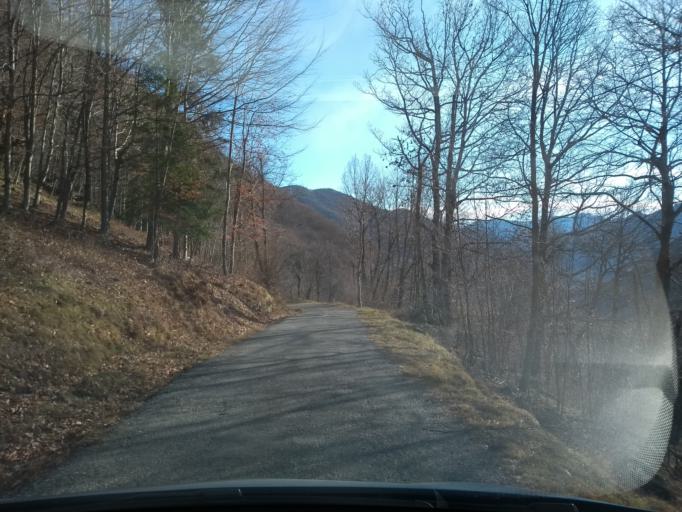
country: IT
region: Piedmont
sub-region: Provincia di Torino
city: Cantoira
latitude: 45.3494
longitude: 7.3830
